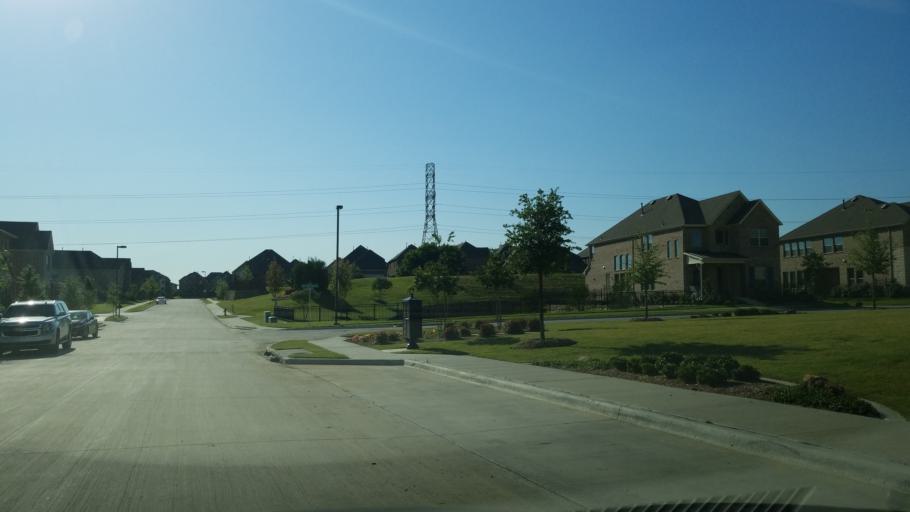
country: US
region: Texas
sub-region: Dallas County
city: Coppell
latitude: 32.9034
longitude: -96.9939
